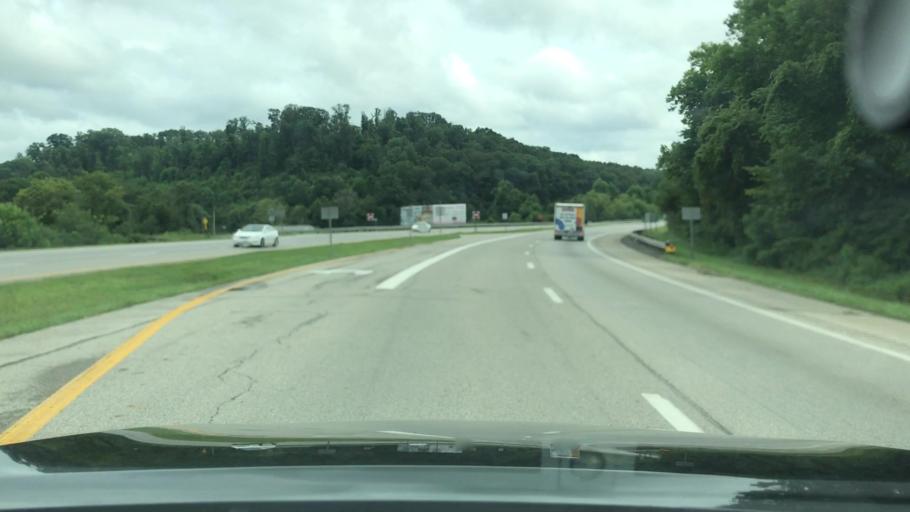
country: US
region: Ohio
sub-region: Jackson County
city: Jackson
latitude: 39.1305
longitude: -82.7032
